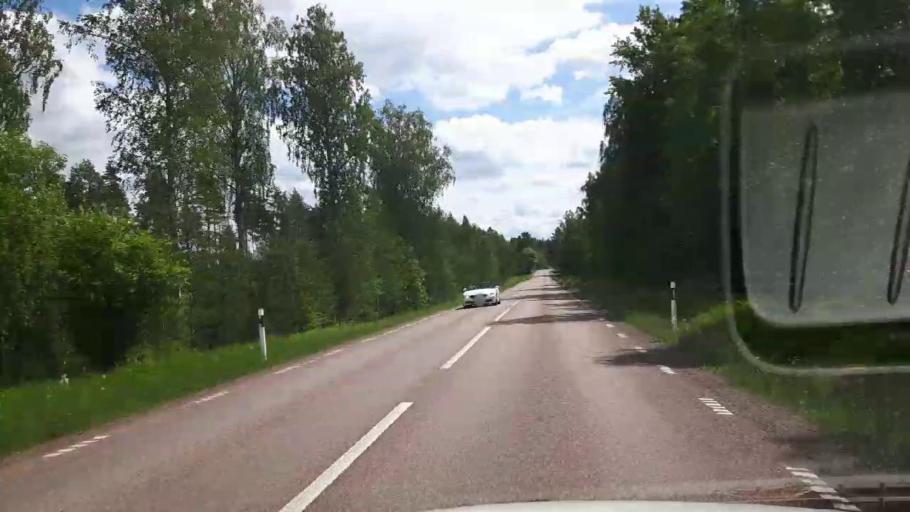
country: SE
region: Dalarna
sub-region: Saters Kommun
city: Saeter
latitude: 60.4130
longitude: 15.8526
